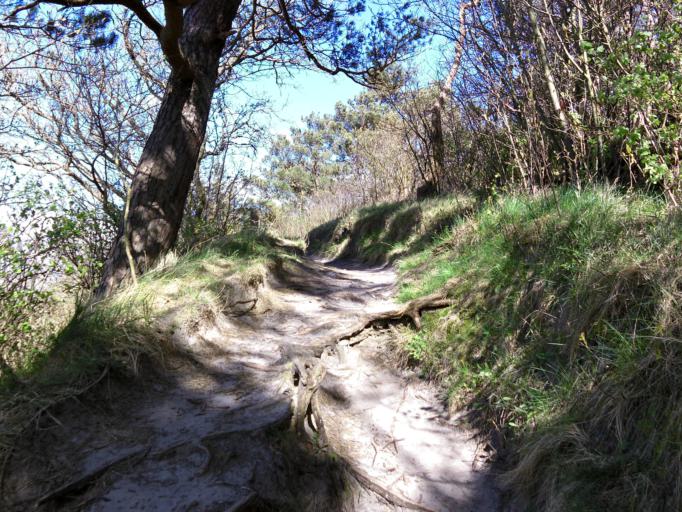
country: DE
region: Mecklenburg-Vorpommern
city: Hiddensee
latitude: 54.5951
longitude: 13.1089
